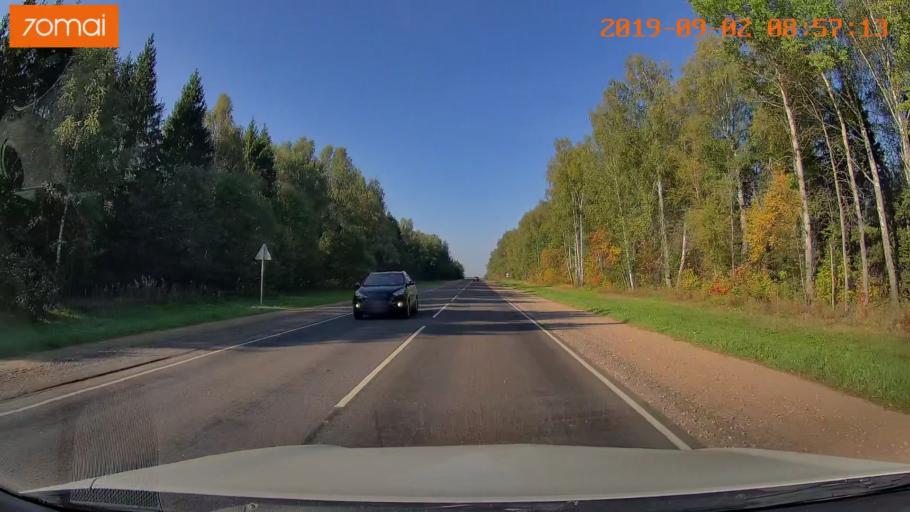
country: RU
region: Kaluga
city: Medyn'
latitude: 54.9387
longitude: 35.7736
